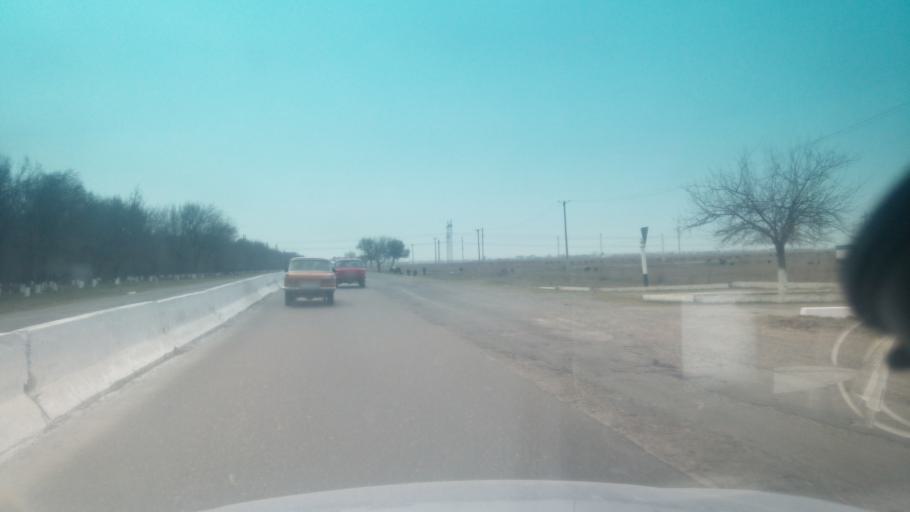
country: UZ
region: Sirdaryo
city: Yangiyer
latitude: 40.2558
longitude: 68.8341
